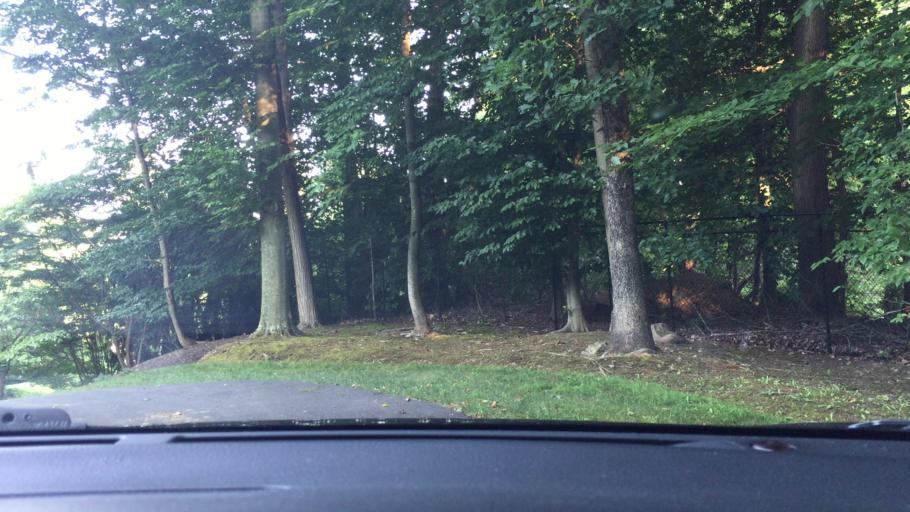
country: US
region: Maryland
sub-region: Montgomery County
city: Potomac
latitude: 39.0146
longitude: -77.1765
